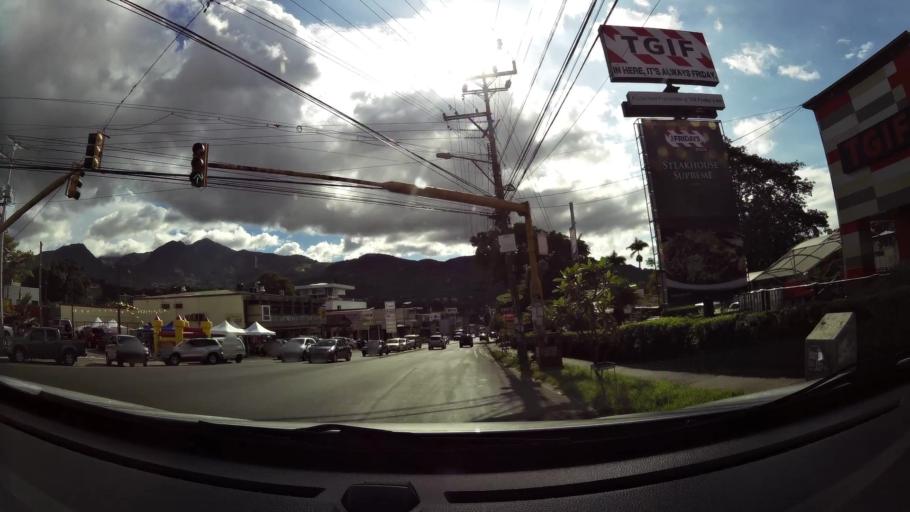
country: CR
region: San Jose
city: San Rafael
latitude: 9.9324
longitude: -84.1295
